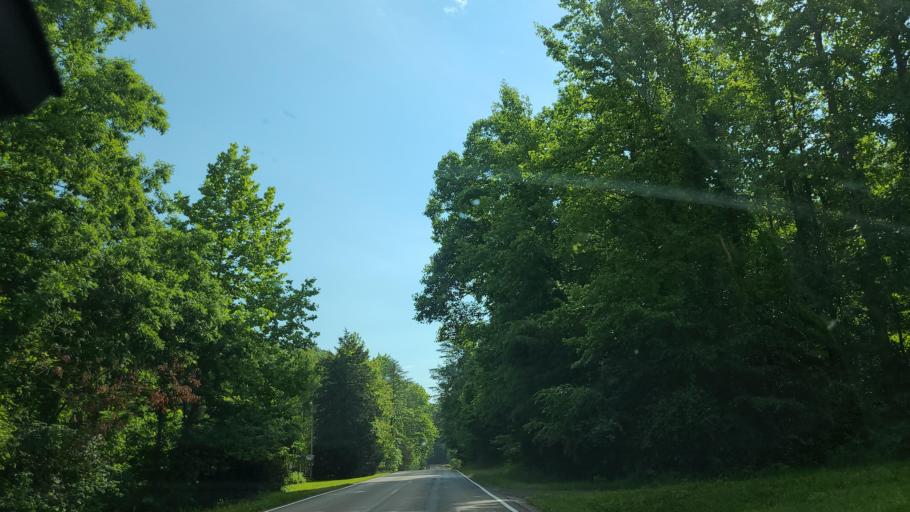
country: US
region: Kentucky
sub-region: Bell County
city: Middlesboro
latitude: 36.6891
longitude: -83.8739
